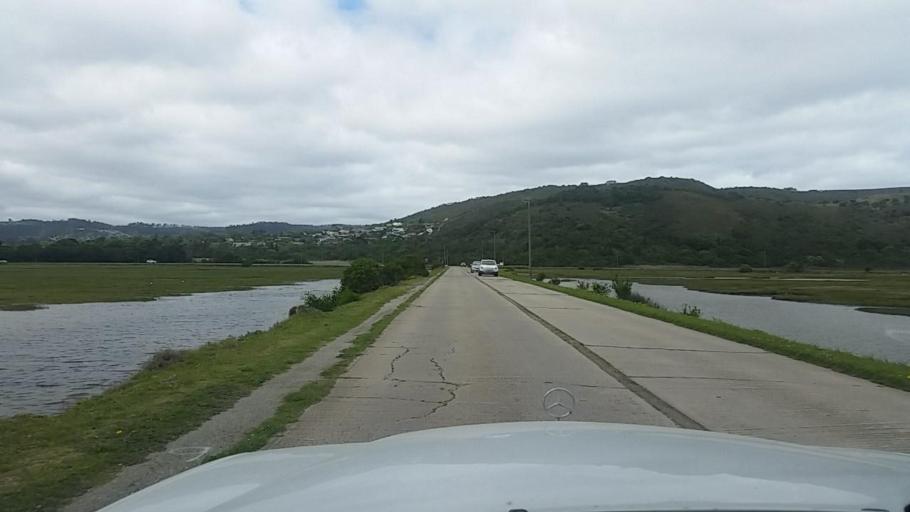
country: ZA
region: Western Cape
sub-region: Eden District Municipality
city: Knysna
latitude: -34.0663
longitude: 23.0676
